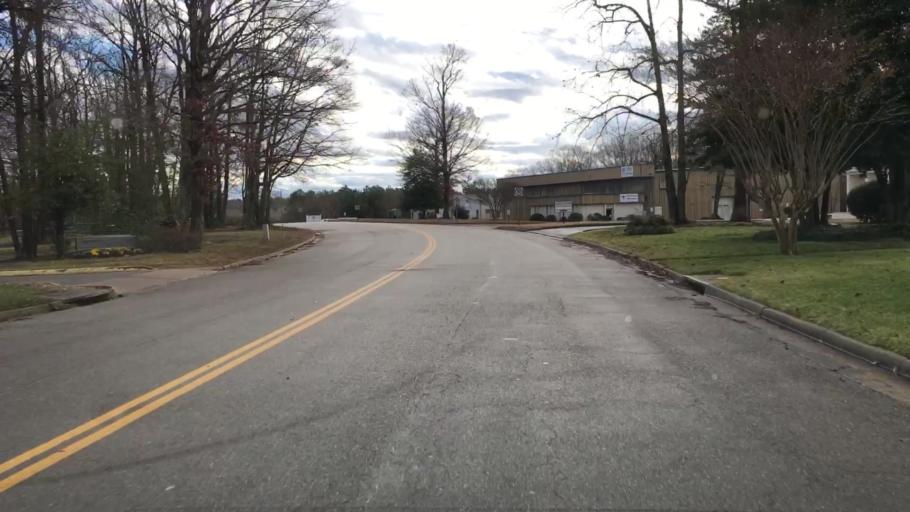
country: US
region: Virginia
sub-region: Chesterfield County
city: Bon Air
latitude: 37.5000
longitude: -77.5951
